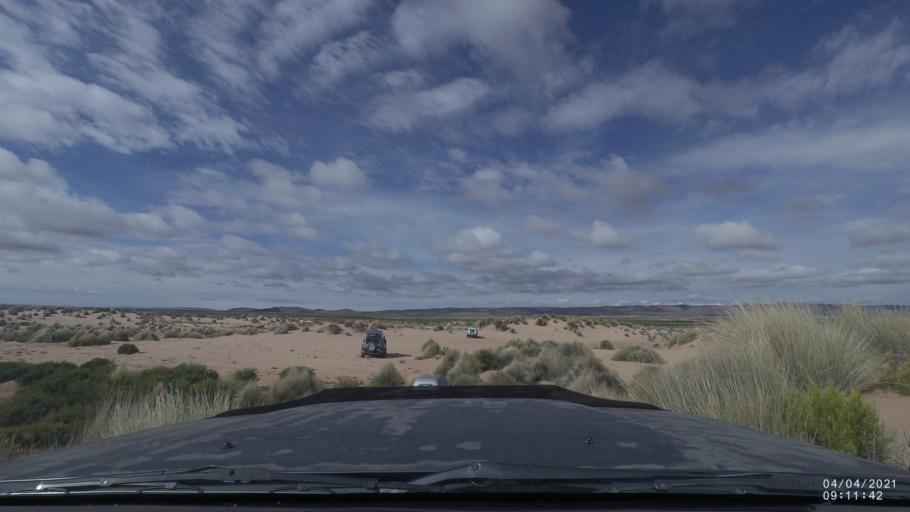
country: BO
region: Oruro
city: Poopo
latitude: -18.7135
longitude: -67.4816
